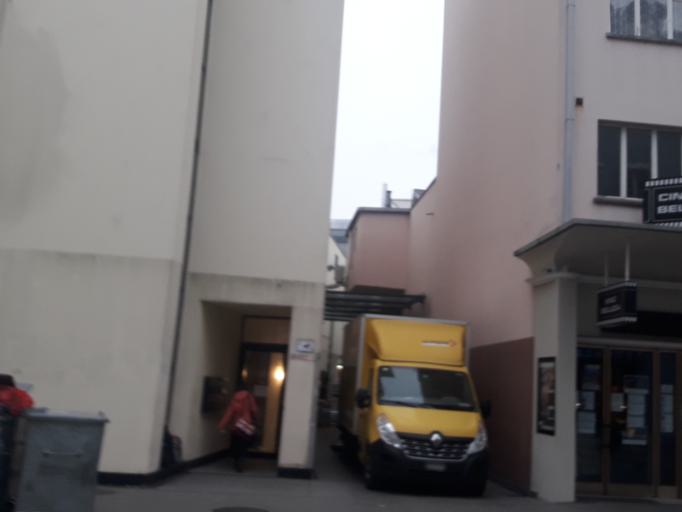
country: CH
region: Bern
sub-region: Biel/Bienne District
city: Biel/Bienne
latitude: 47.1386
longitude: 7.2456
